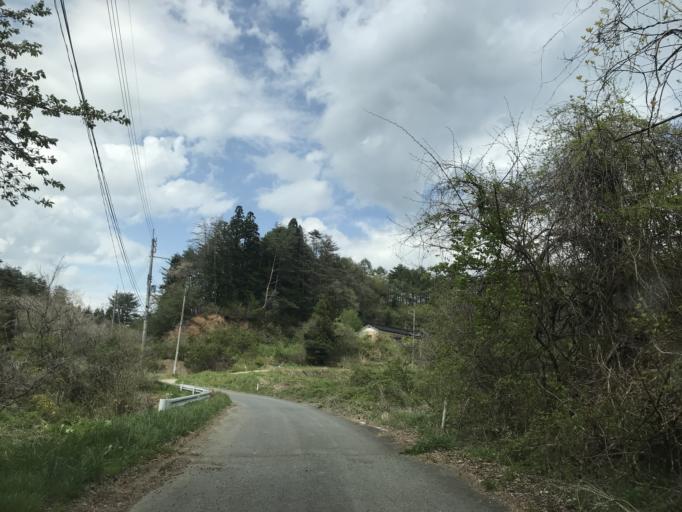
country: JP
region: Iwate
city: Ichinoseki
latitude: 38.7802
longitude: 141.4311
